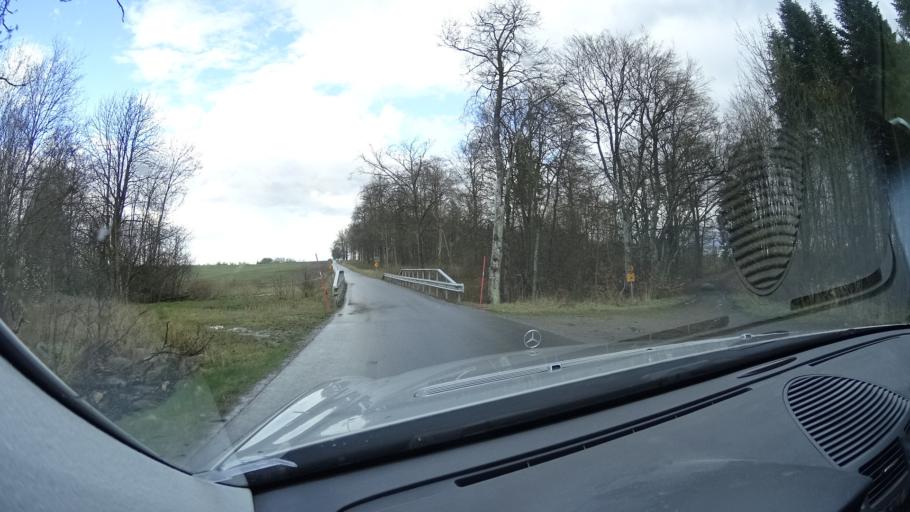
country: SE
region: Skane
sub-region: Eslovs Kommun
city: Eslov
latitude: 55.8153
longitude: 13.2962
